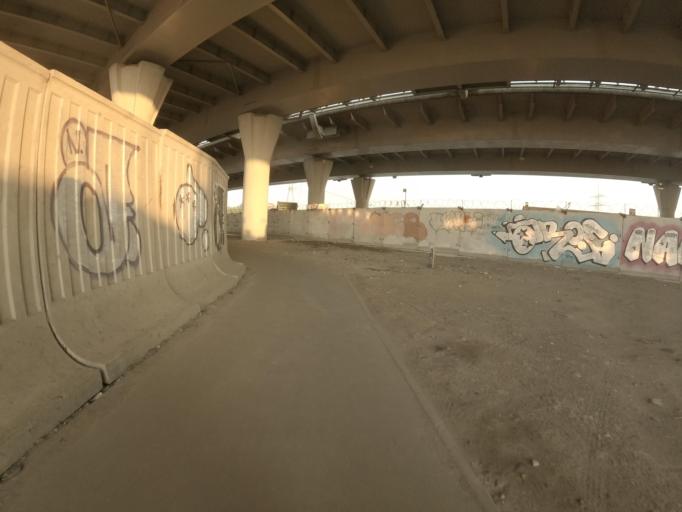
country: RU
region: St.-Petersburg
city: Avtovo
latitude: 59.8807
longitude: 30.2891
